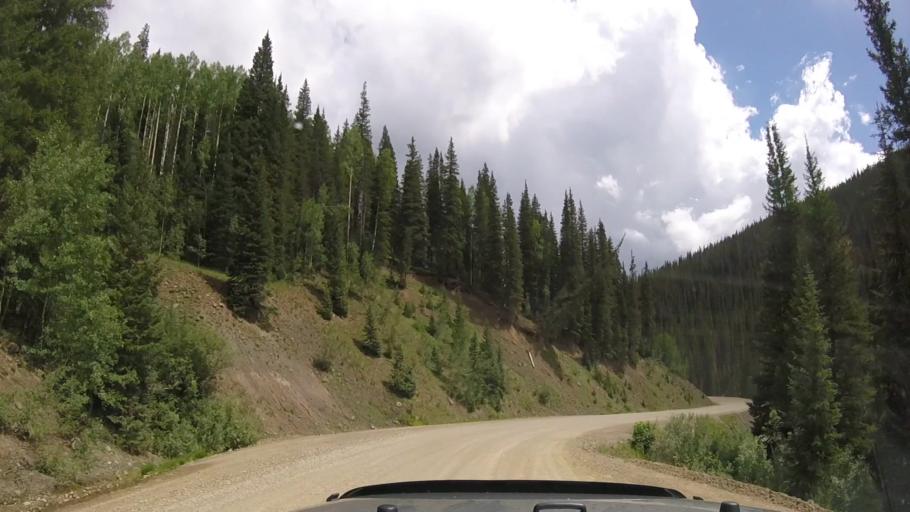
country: US
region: Colorado
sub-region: San Juan County
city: Silverton
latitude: 37.8364
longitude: -107.6776
